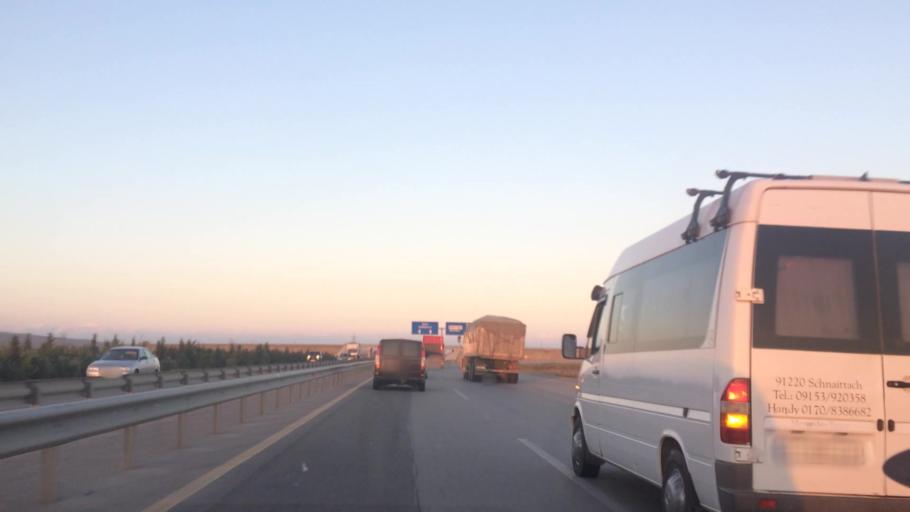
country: AZ
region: Baki
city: Qobustan
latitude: 39.9517
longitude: 49.3730
